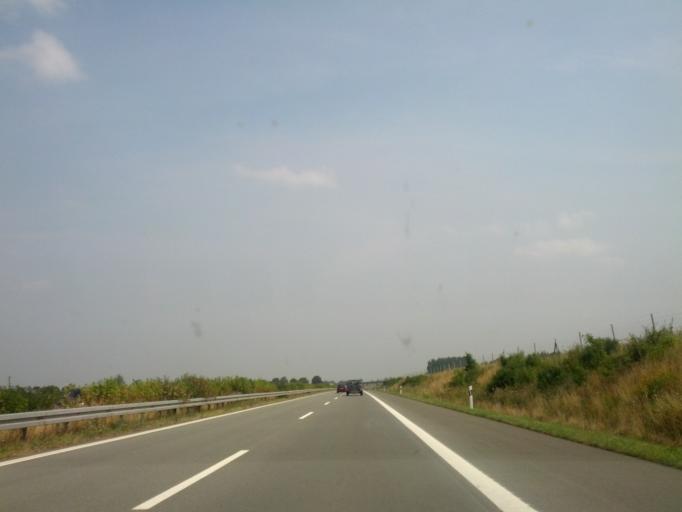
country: DE
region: Mecklenburg-Vorpommern
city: Tribsees
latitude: 54.0835
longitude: 12.7807
